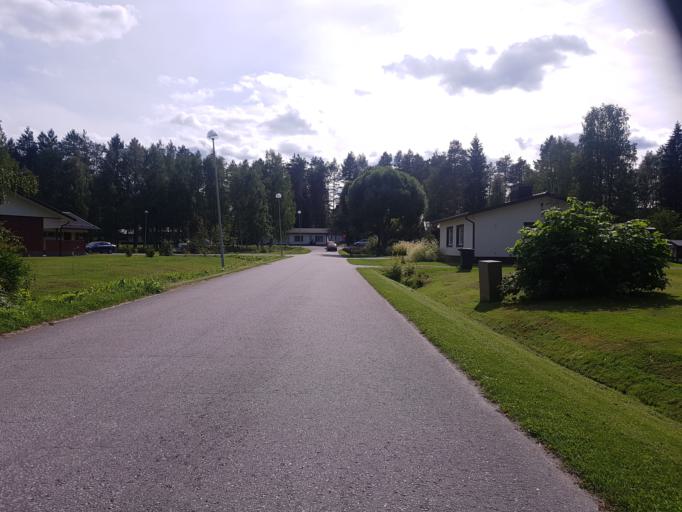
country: FI
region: Kainuu
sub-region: Kehys-Kainuu
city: Kuhmo
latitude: 64.1225
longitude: 29.5260
